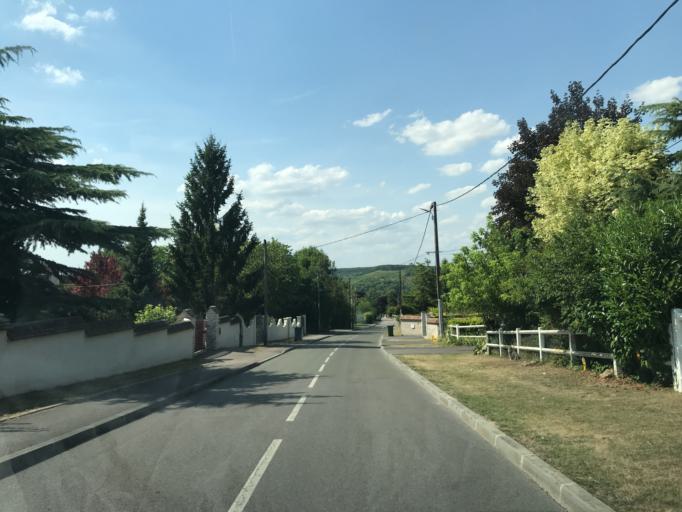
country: FR
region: Haute-Normandie
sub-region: Departement de l'Eure
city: Gasny
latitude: 49.0718
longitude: 1.5978
